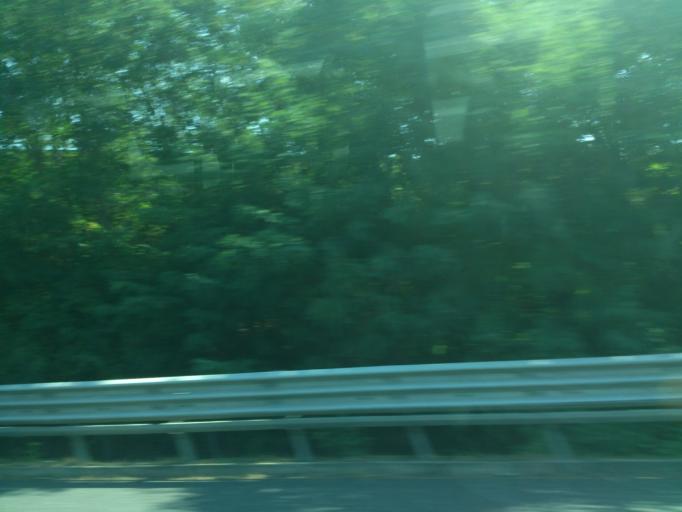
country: IT
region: Calabria
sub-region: Provincia di Vibo-Valentia
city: Francavilla Angitola
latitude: 38.7994
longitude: 16.2282
